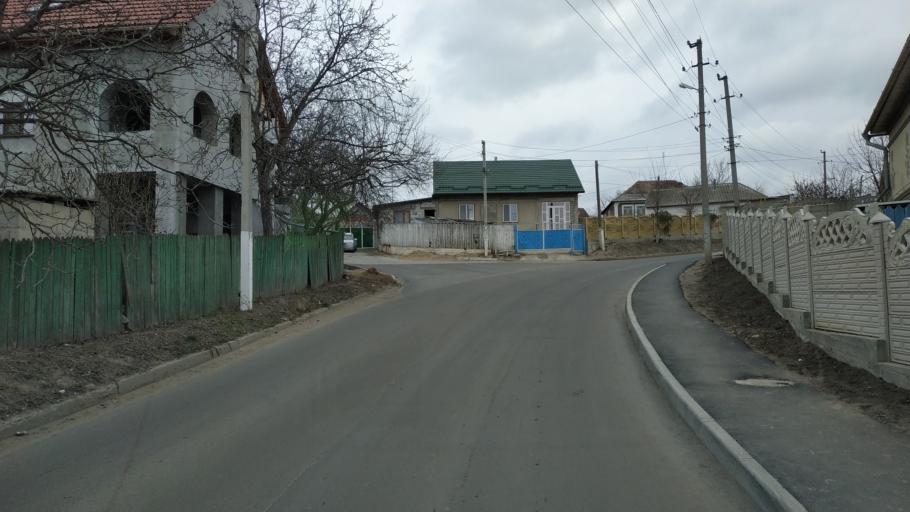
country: MD
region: Laloveni
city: Ialoveni
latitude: 46.8672
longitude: 28.7609
